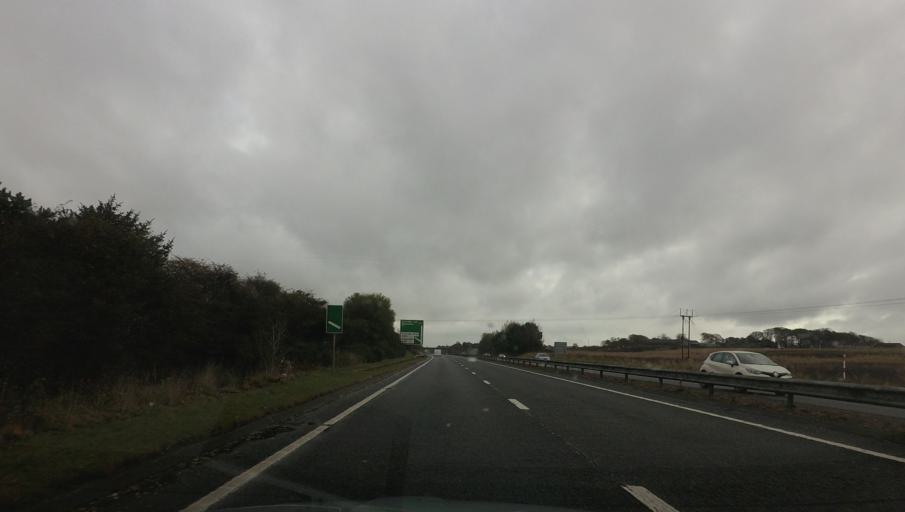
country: GB
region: Scotland
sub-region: Fife
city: Cardenden
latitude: 56.1361
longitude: -3.2193
